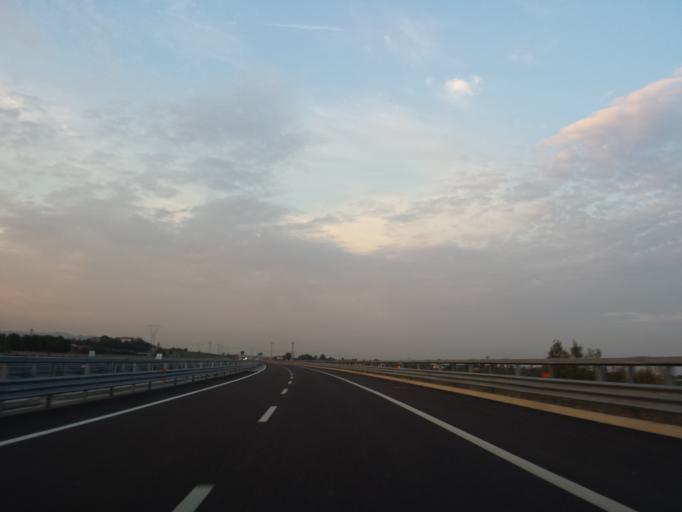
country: IT
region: Veneto
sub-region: Provincia di Vicenza
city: Albettone
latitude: 45.3651
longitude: 11.6088
